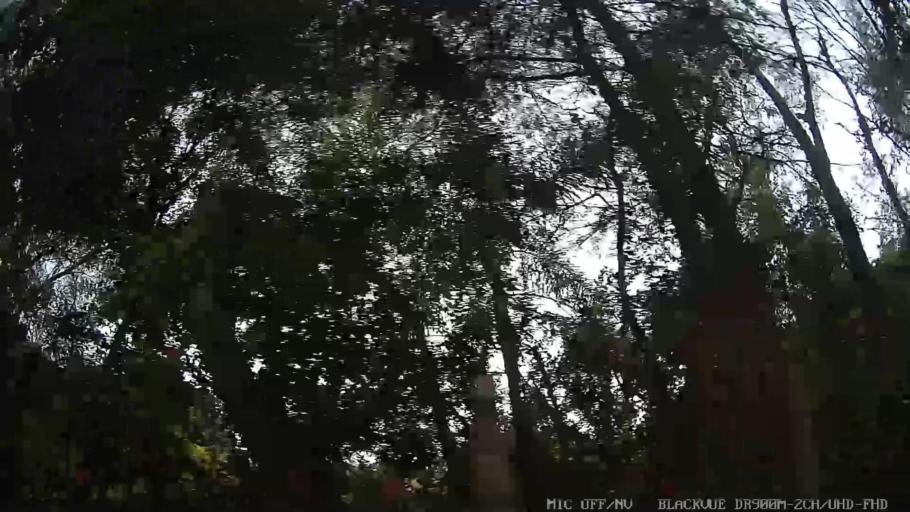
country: BR
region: Sao Paulo
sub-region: Itatiba
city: Itatiba
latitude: -23.0365
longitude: -46.8946
